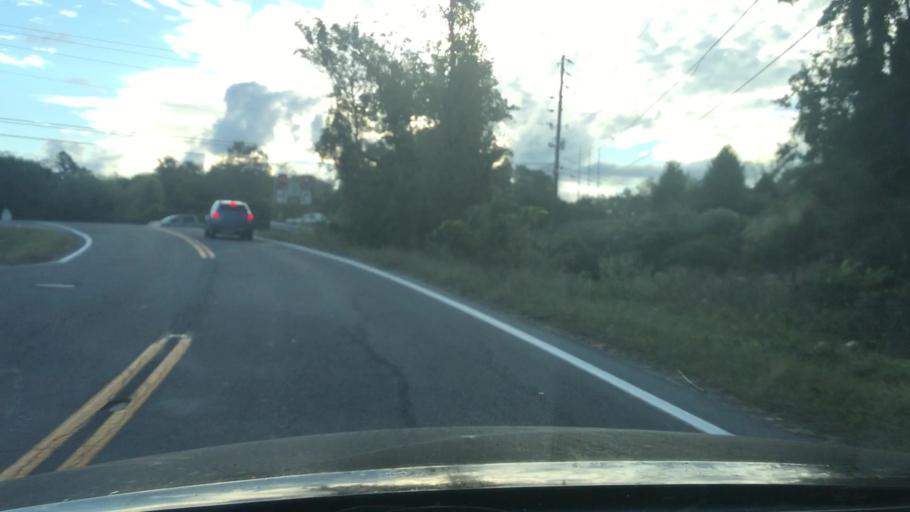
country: US
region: Tennessee
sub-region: Cheatham County
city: Ashland City
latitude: 36.2645
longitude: -87.0596
